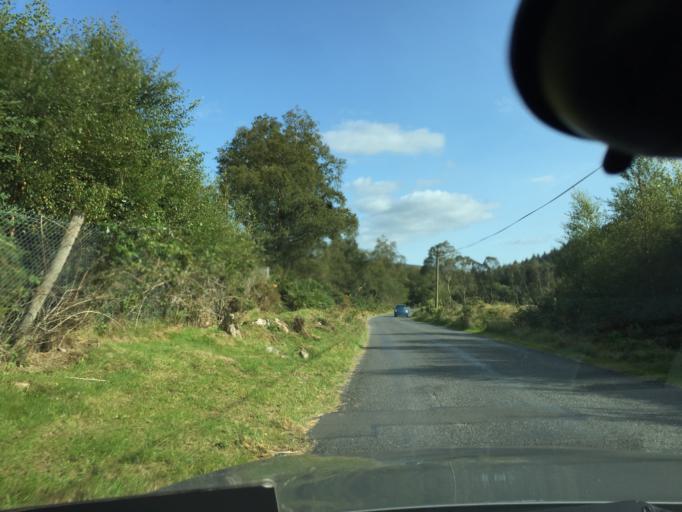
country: IE
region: Leinster
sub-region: Wicklow
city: Rathdrum
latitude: 53.0349
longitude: -6.3192
